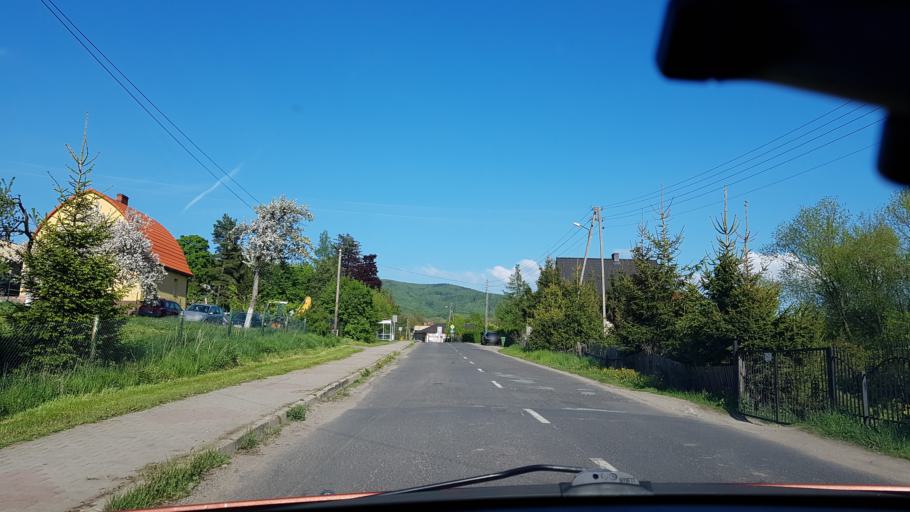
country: PL
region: Lower Silesian Voivodeship
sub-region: Powiat klodzki
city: Jugow
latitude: 50.5892
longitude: 16.5565
